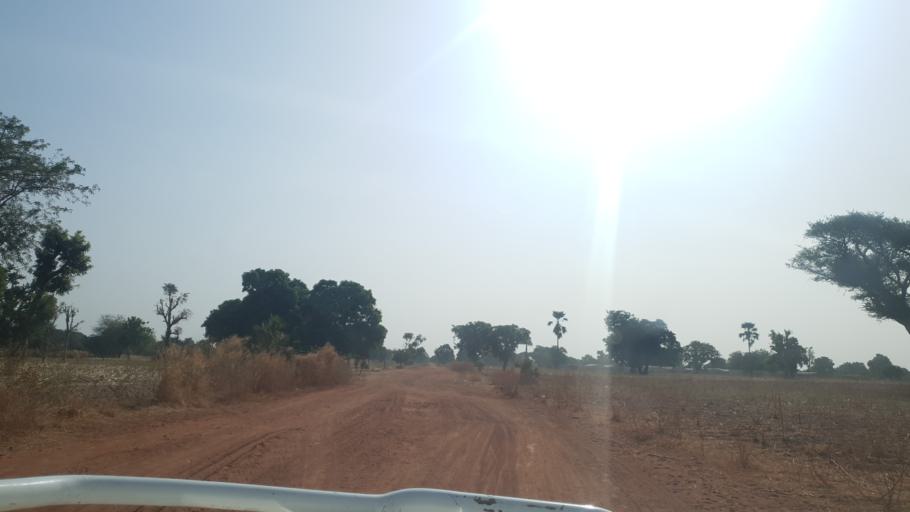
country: ML
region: Koulikoro
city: Dioila
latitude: 12.7069
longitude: -6.7732
